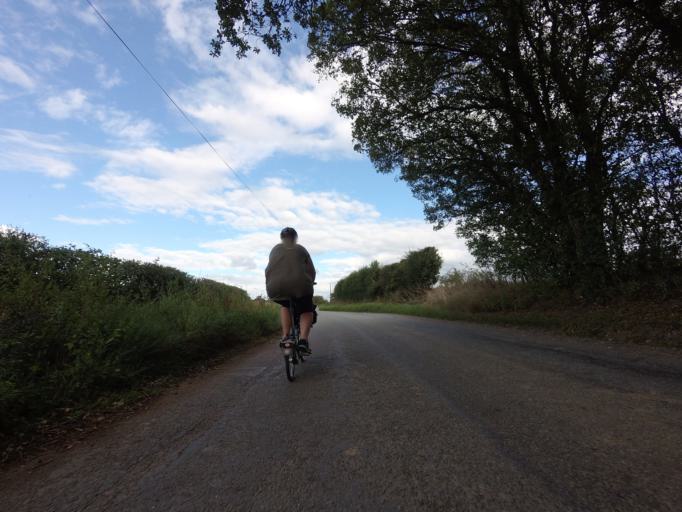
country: GB
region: England
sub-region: Kent
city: Marden
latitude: 51.2107
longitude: 0.5006
